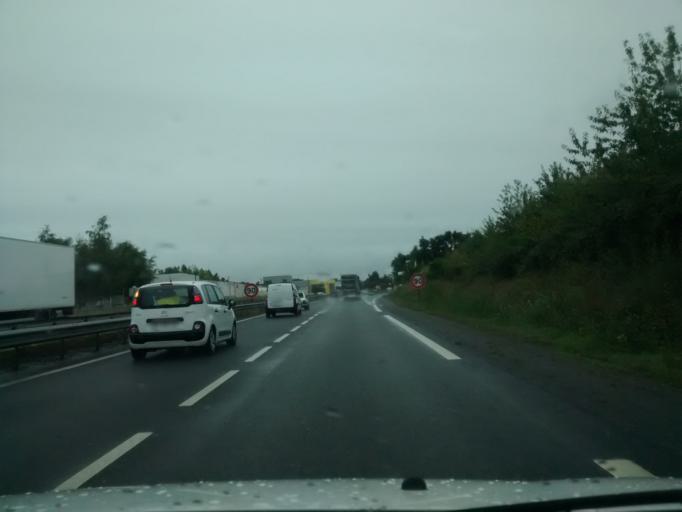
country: FR
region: Brittany
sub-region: Departement d'Ille-et-Vilaine
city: Vern-sur-Seiche
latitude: 48.0543
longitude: -1.6107
